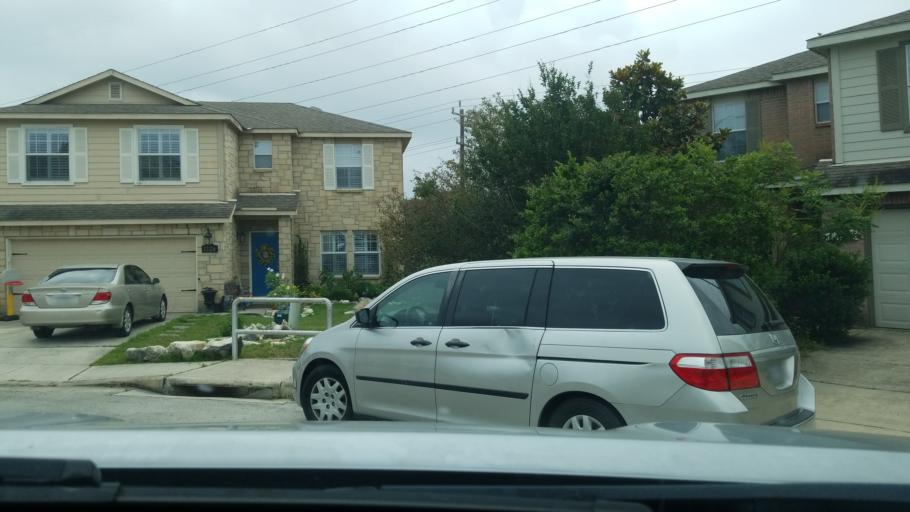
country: US
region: Texas
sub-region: Bexar County
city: Timberwood Park
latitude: 29.6801
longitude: -98.4645
